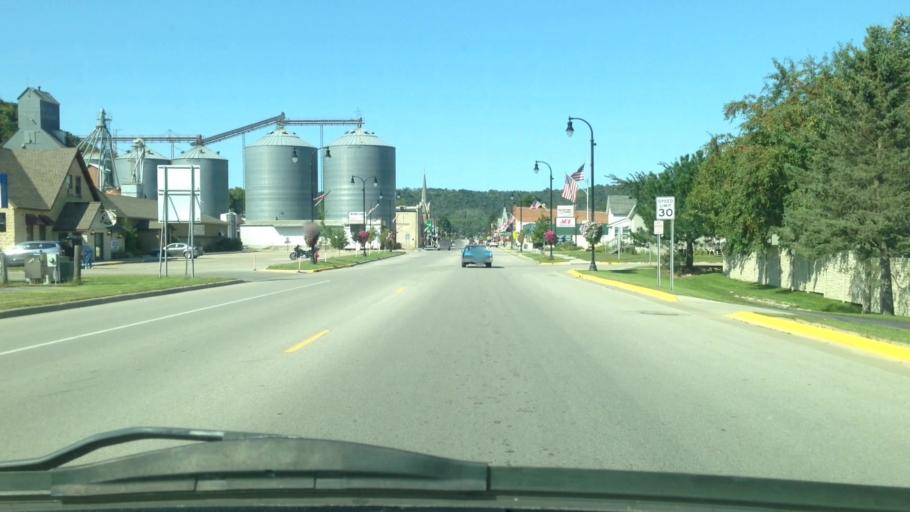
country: US
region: Minnesota
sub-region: Fillmore County
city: Rushford
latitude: 43.8058
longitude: -91.7532
